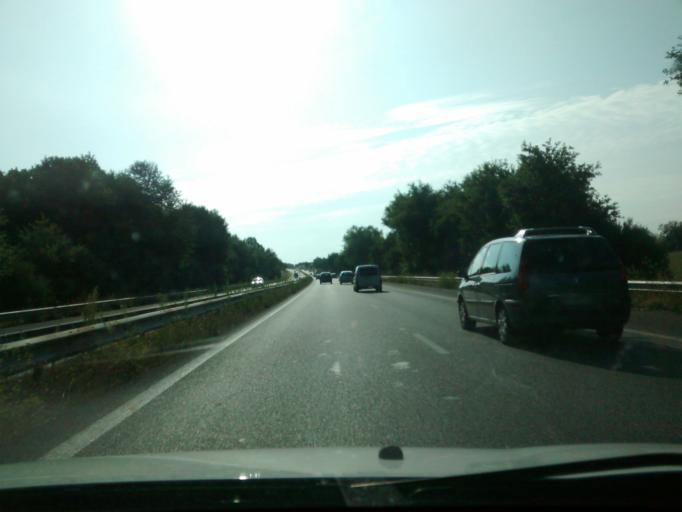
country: FR
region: Brittany
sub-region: Departement d'Ille-et-Vilaine
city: Chateaubourg
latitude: 48.0932
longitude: -1.3934
